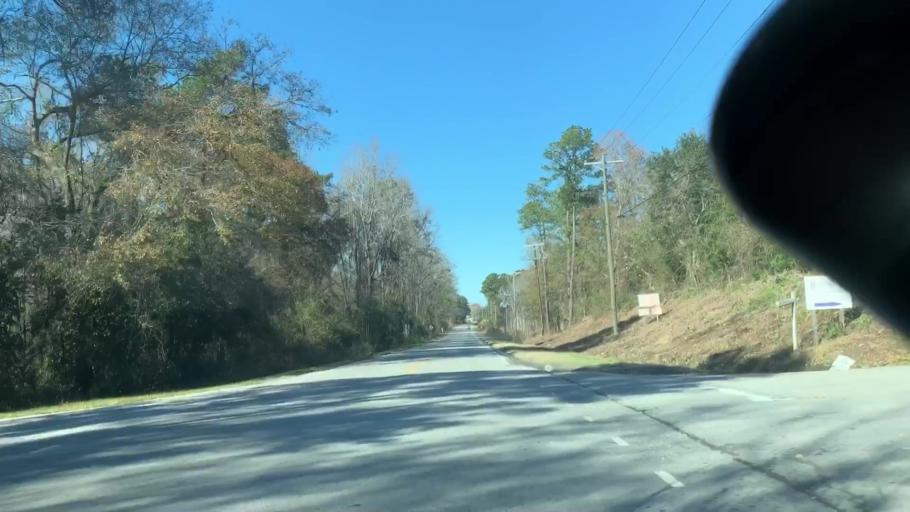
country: US
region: South Carolina
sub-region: Richland County
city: Hopkins
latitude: 33.9219
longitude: -80.9555
